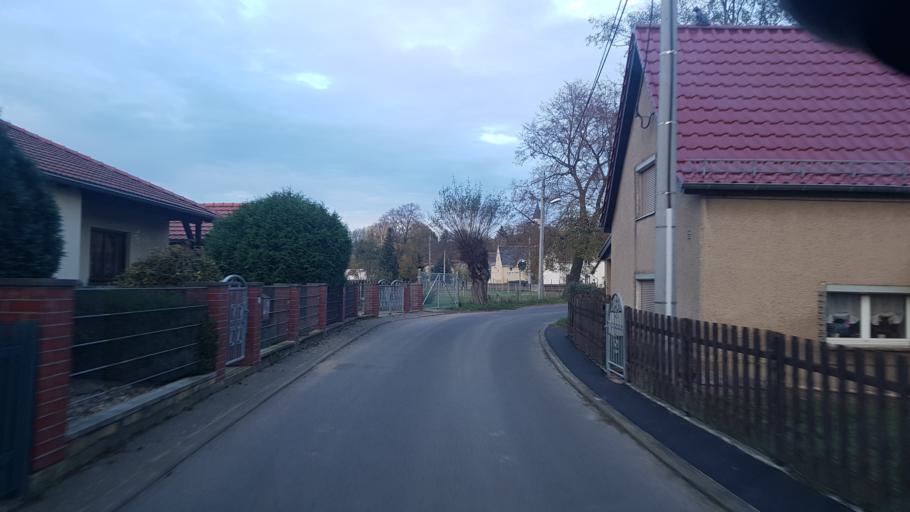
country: DE
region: Saxony
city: Dahlen
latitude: 51.3848
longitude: 13.0391
